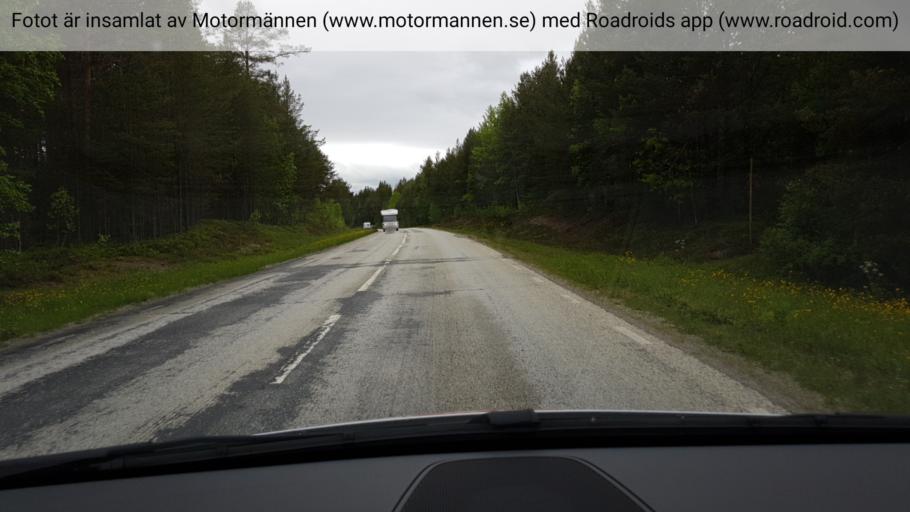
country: SE
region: Jaemtland
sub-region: Harjedalens Kommun
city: Sveg
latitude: 62.4124
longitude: 13.6737
